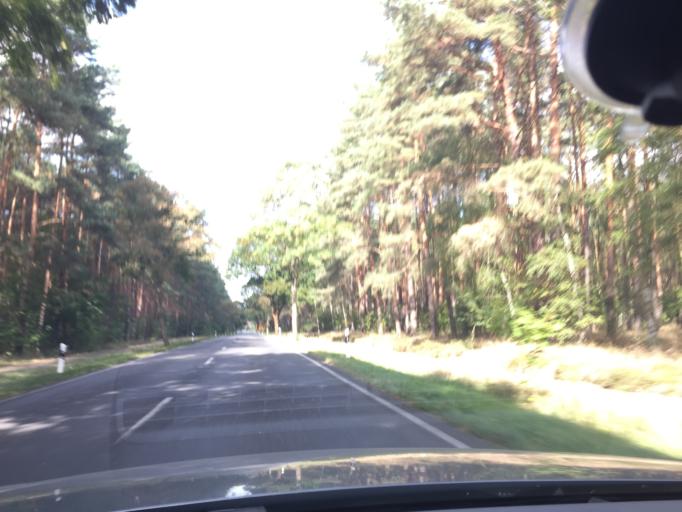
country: DE
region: Brandenburg
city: Grunheide
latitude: 52.3873
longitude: 13.8281
